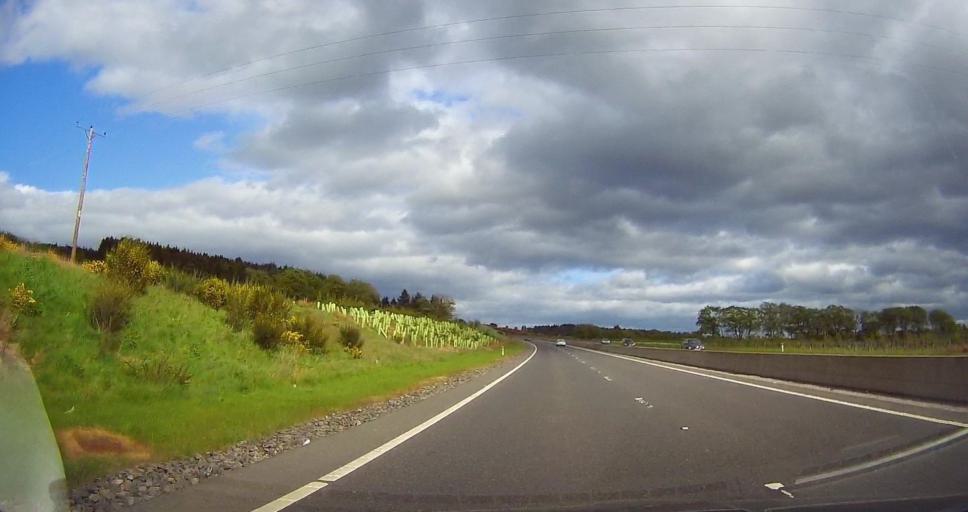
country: GB
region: Scotland
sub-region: Aberdeen City
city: Cults
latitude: 57.0780
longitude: -2.2060
